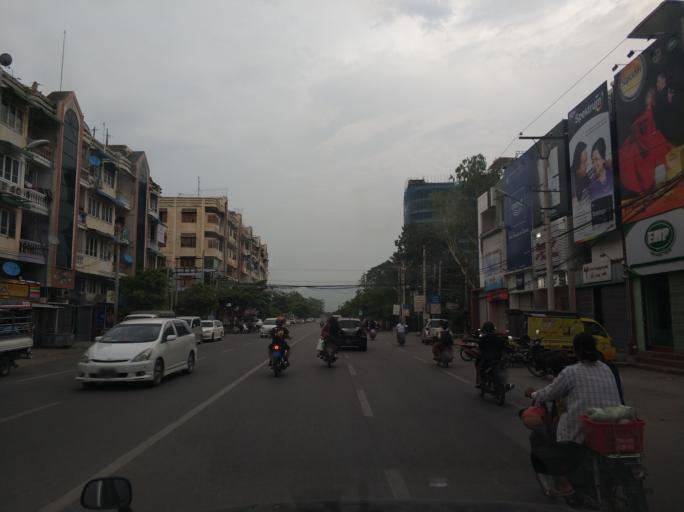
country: MM
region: Mandalay
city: Mandalay
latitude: 21.9757
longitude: 96.1074
